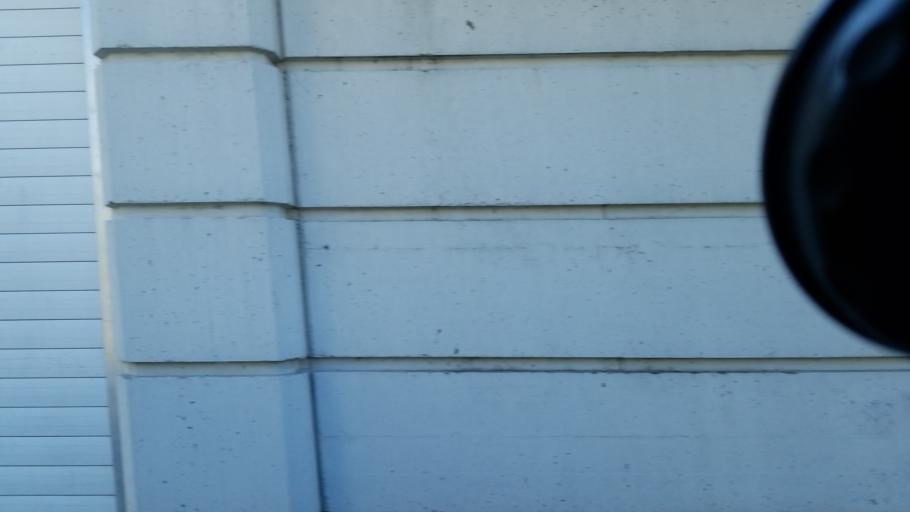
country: AL
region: Shkoder
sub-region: Rrethi i Shkodres
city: Shkoder
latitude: 42.0691
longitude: 19.5224
